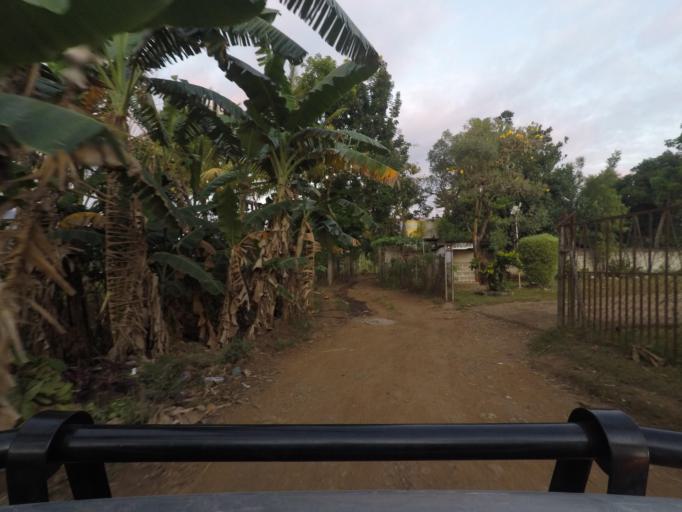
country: TL
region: Bobonaro
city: Maliana
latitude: -8.9871
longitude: 125.2102
